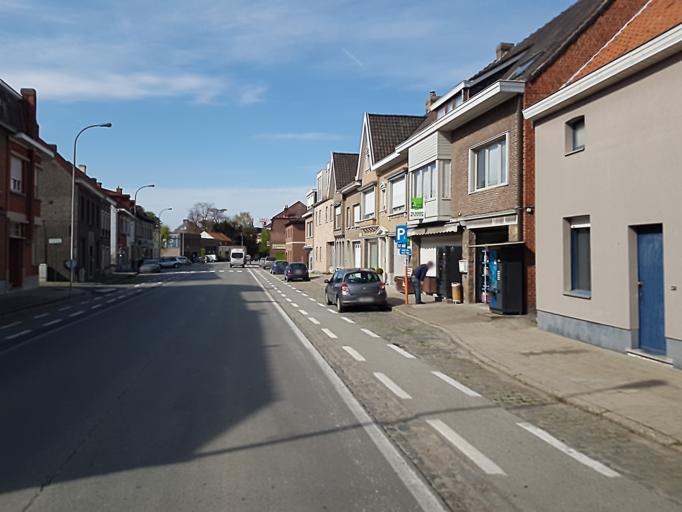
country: BE
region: Flanders
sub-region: Provincie West-Vlaanderen
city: Waregem
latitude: 50.8390
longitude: 3.4070
